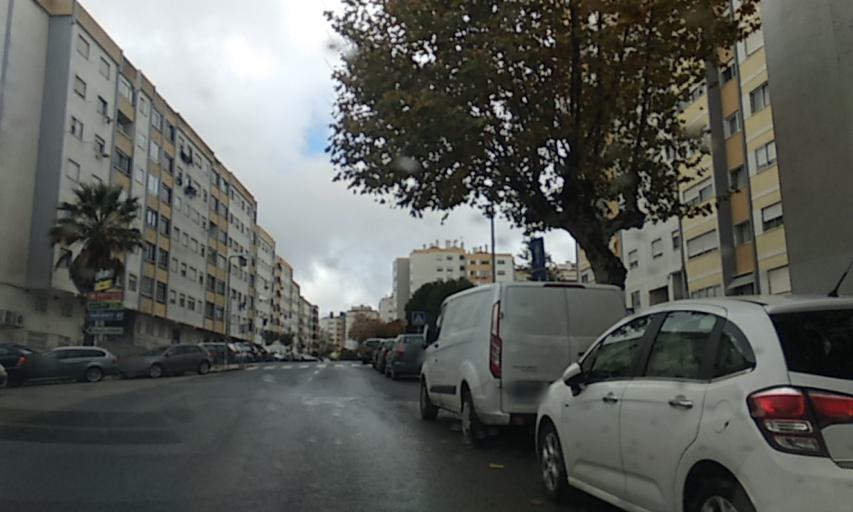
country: PT
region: Lisbon
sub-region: Sintra
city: Cacem
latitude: 38.7544
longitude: -9.2828
